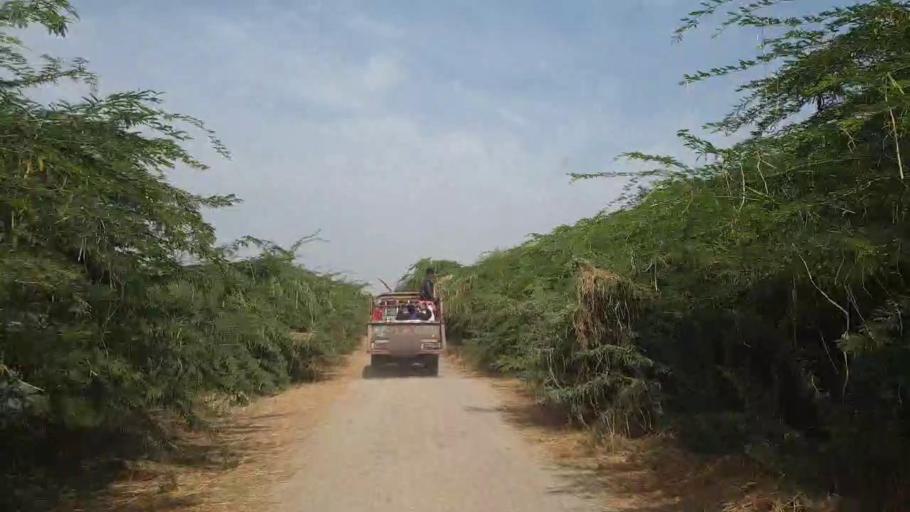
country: PK
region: Sindh
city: Tando Bago
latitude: 24.9153
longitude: 68.9954
